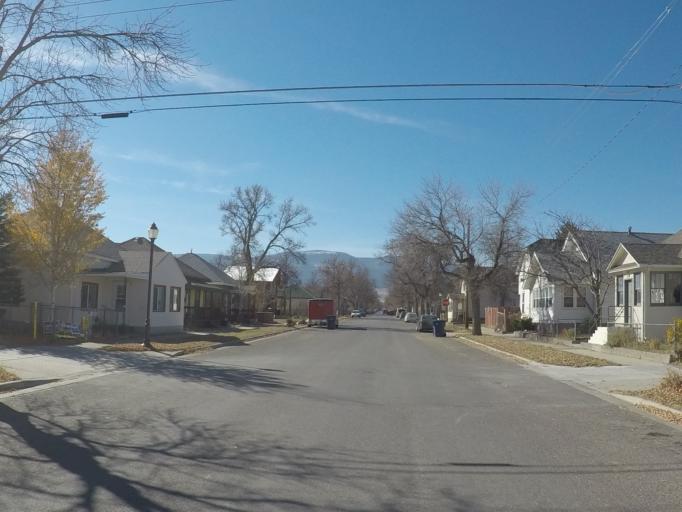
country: US
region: Montana
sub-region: Park County
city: Livingston
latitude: 45.6661
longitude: -110.5514
